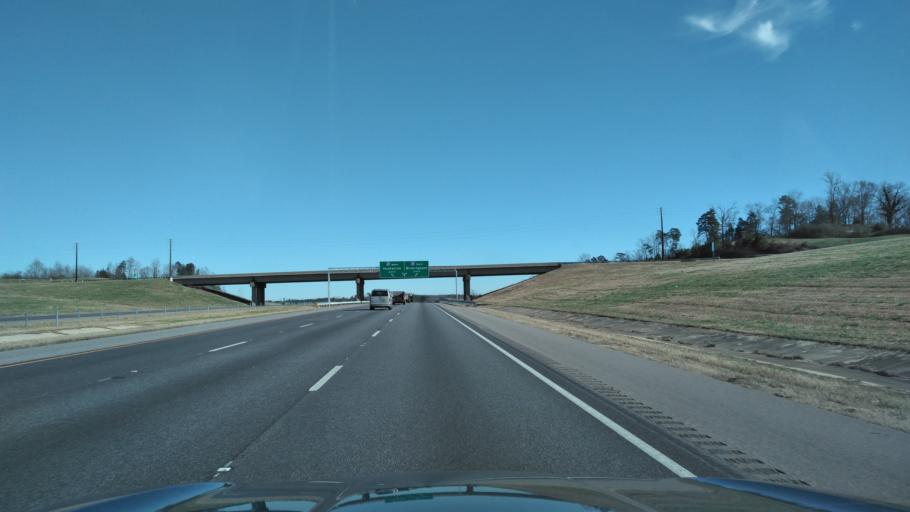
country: US
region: Alabama
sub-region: Jefferson County
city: Forestdale
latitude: 33.5889
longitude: -86.8580
